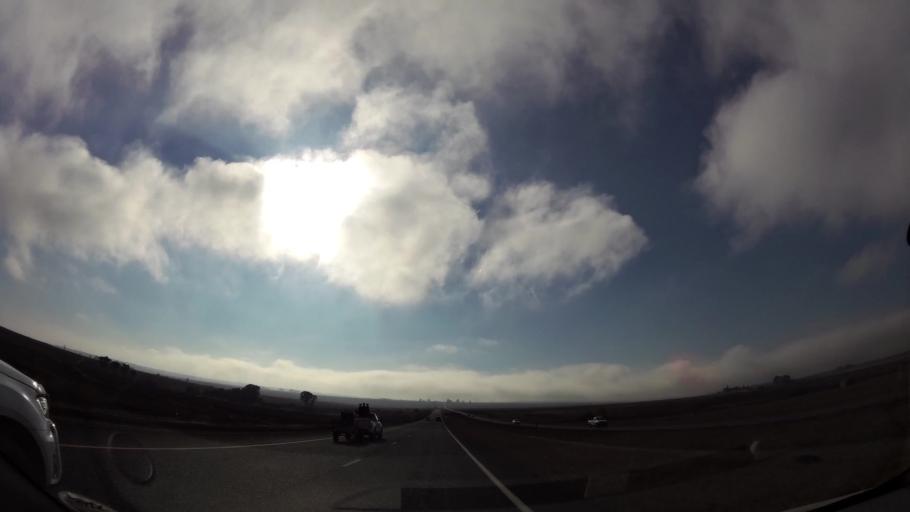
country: ZA
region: Mpumalanga
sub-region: Nkangala District Municipality
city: Delmas
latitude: -26.0341
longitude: 28.8591
